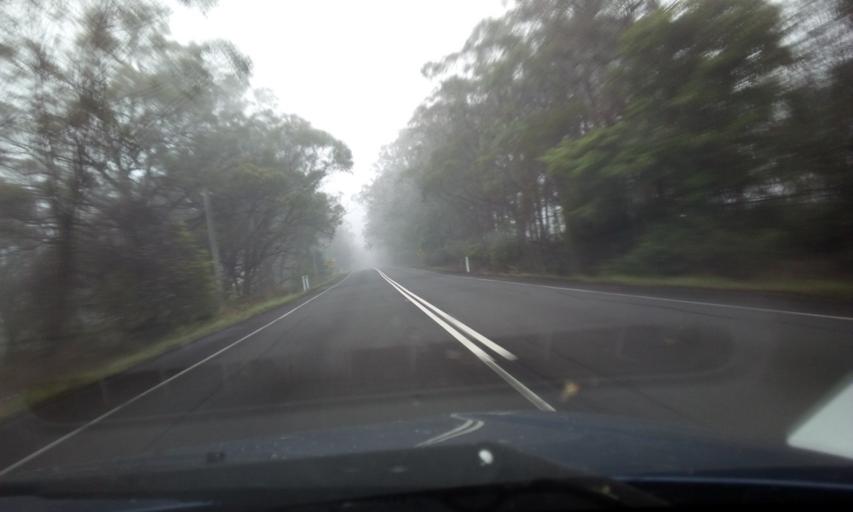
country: AU
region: New South Wales
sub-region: Wollondilly
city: Douglas Park
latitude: -34.2435
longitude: 150.7275
